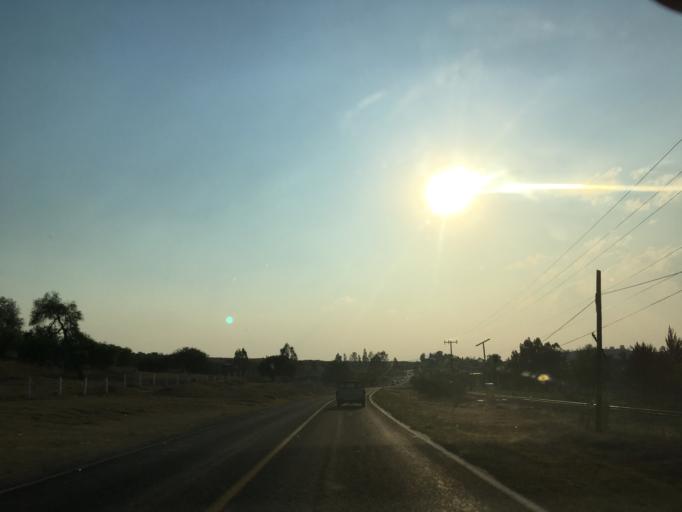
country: MX
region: Michoacan
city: Charo
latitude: 19.7358
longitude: -101.0870
